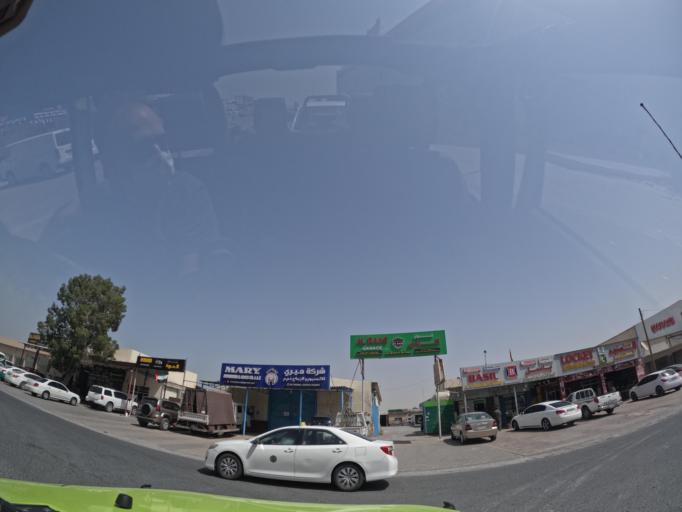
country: AE
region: Umm al Qaywayn
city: Umm al Qaywayn
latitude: 25.5035
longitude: 55.5511
